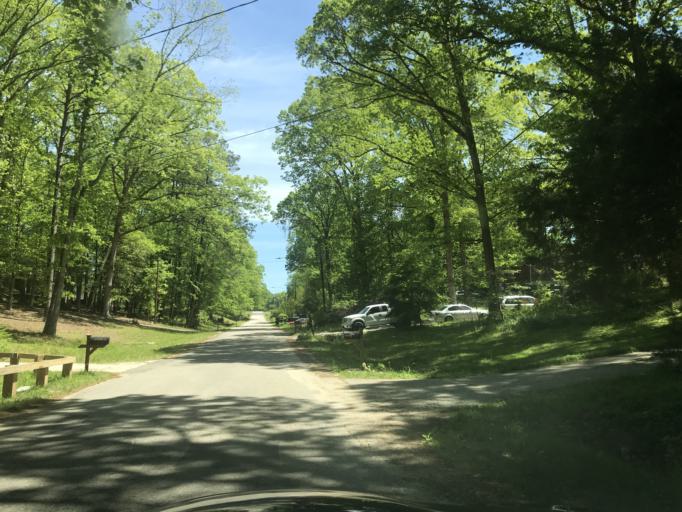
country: US
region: North Carolina
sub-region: Wake County
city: Raleigh
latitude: 35.8270
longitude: -78.5745
